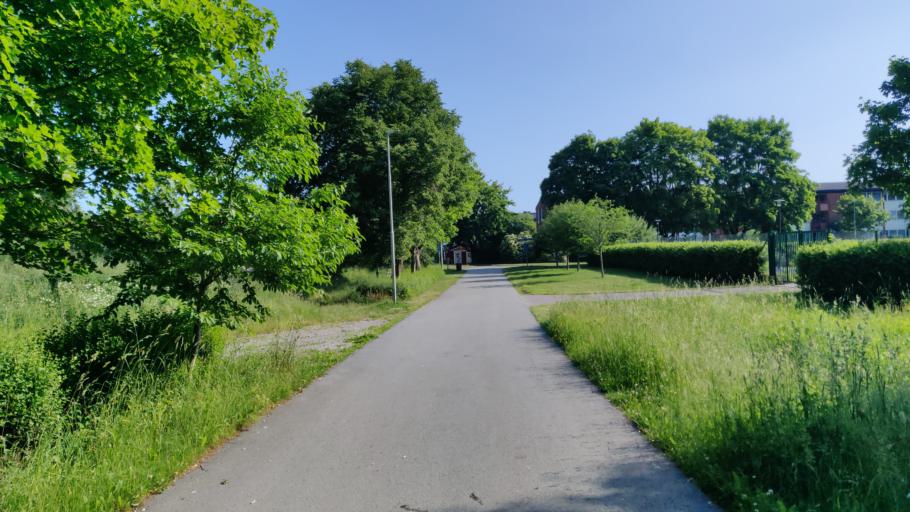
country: SE
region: OErebro
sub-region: Orebro Kommun
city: Orebro
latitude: 59.2879
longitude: 15.1662
